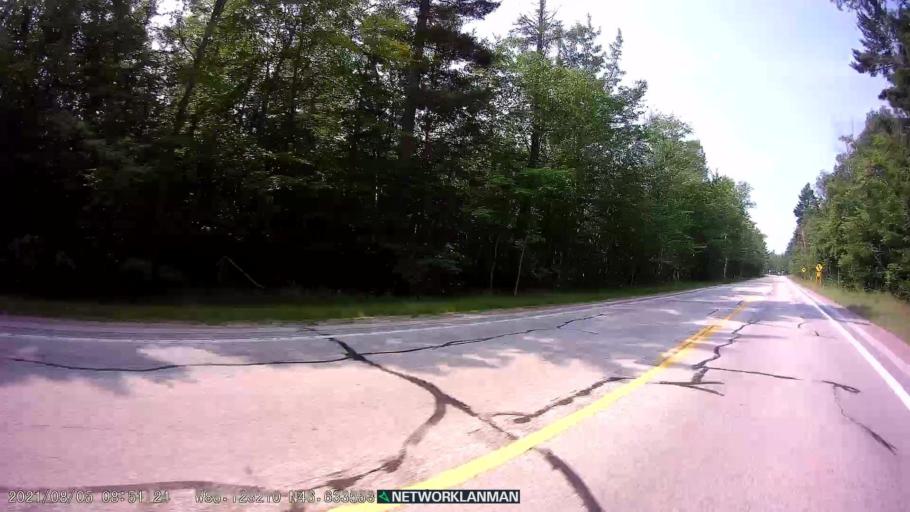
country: US
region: Michigan
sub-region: Luce County
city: Newberry
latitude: 46.6336
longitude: -85.1247
